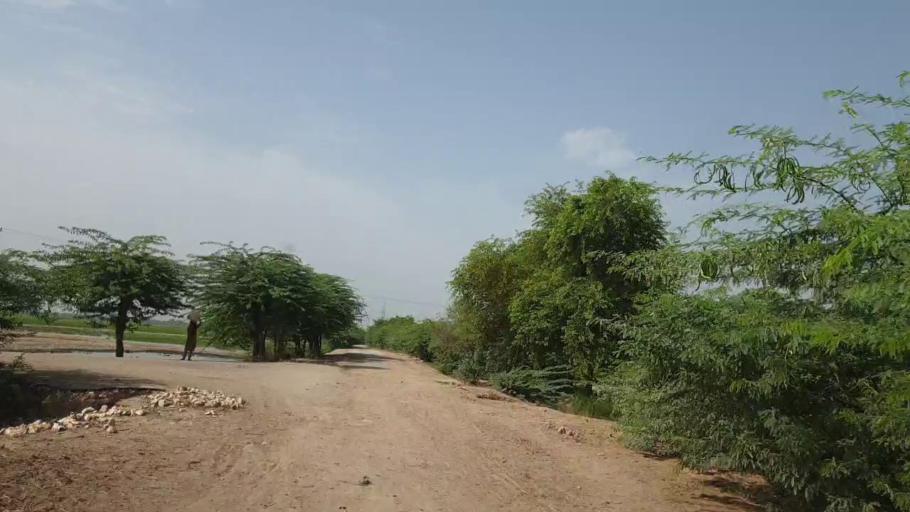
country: PK
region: Sindh
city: Lakhi
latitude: 27.8055
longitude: 68.7181
